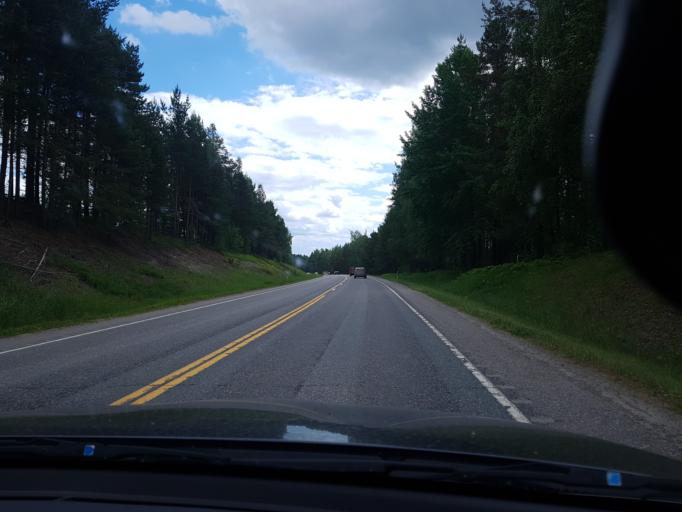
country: FI
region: Pirkanmaa
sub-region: Tampere
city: Paelkaene
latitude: 61.3130
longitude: 24.2867
